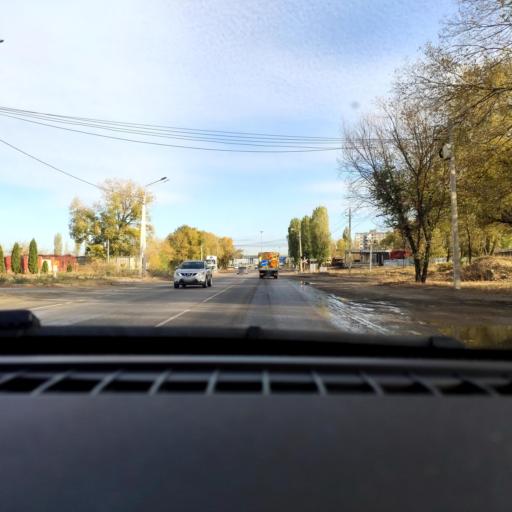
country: RU
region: Voronezj
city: Maslovka
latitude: 51.6438
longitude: 39.2962
